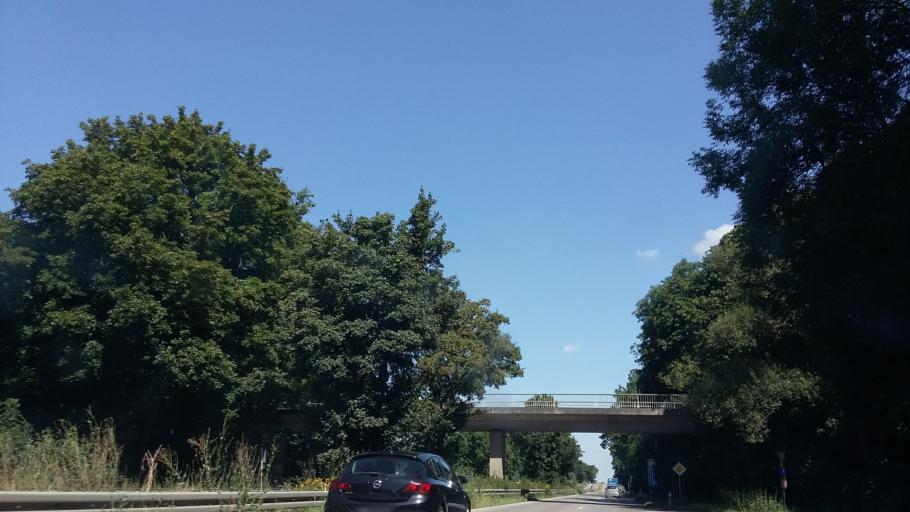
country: DE
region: Bavaria
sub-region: Swabia
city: Augsburg
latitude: 48.4025
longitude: 10.9205
